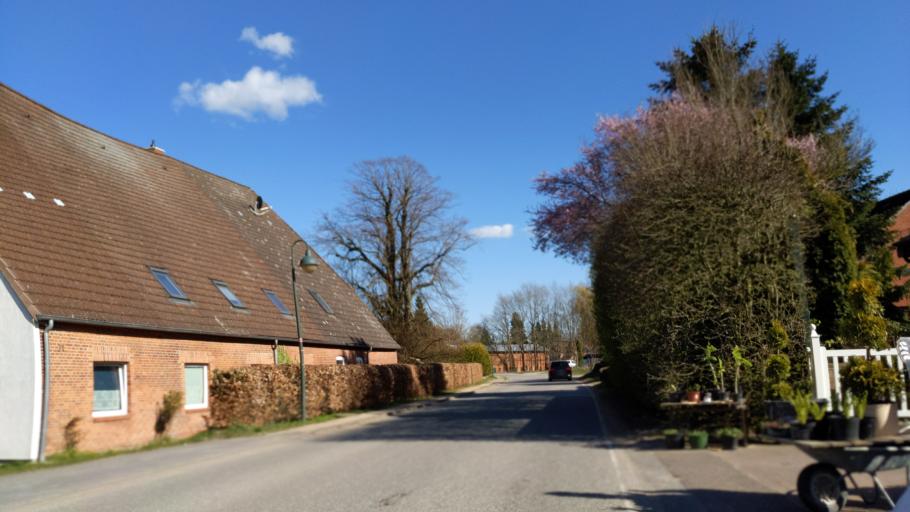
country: DE
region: Schleswig-Holstein
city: Eutin
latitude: 54.0759
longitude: 10.6245
